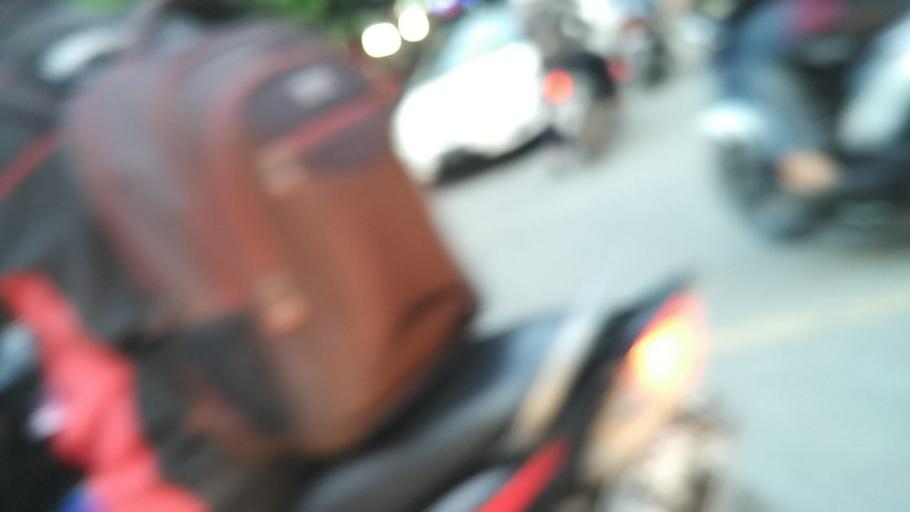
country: ID
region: Central Java
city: Semarang
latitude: -6.9796
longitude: 110.4607
